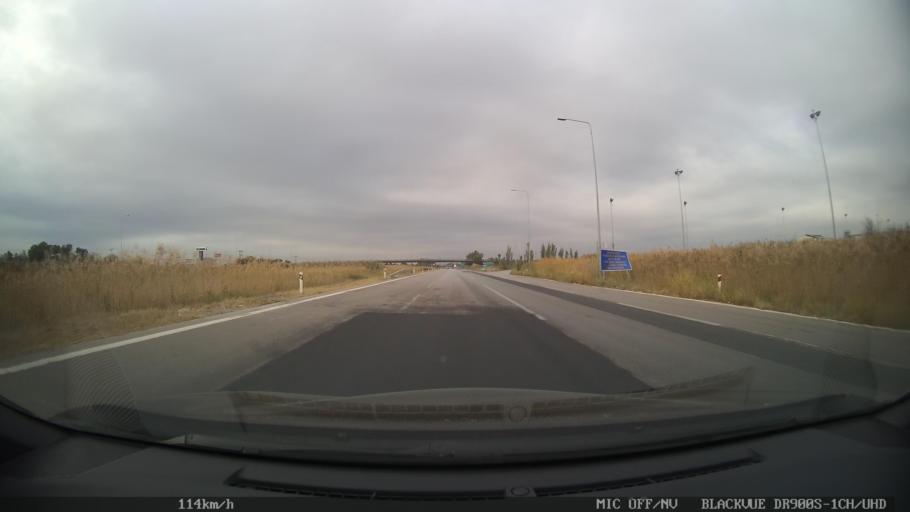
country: GR
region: Central Macedonia
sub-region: Nomos Thessalonikis
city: Chalastra
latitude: 40.6158
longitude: 22.7460
